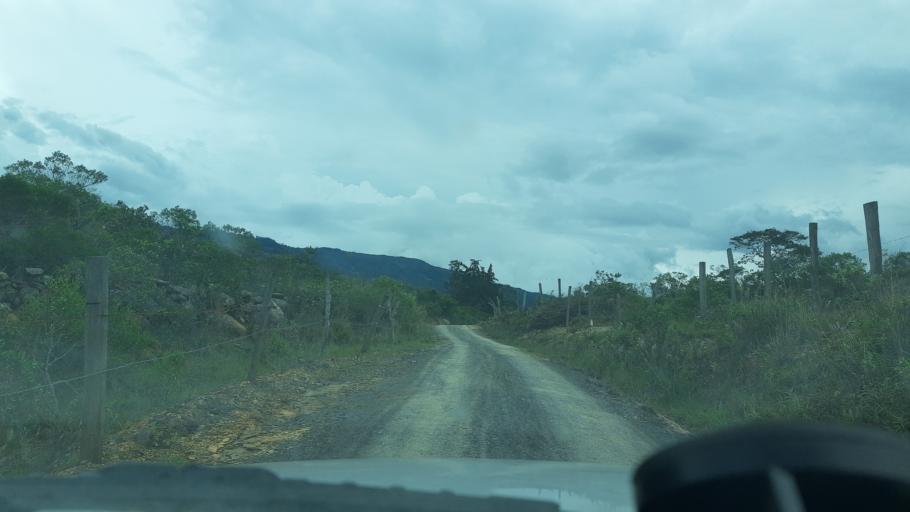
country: CO
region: Boyaca
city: Santa Sofia
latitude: 5.7063
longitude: -73.5840
